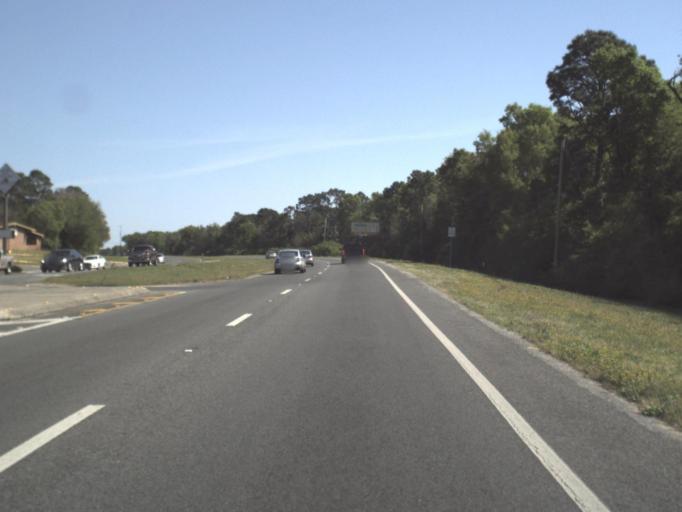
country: US
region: Florida
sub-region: Escambia County
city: Bellview
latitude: 30.4576
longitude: -87.2993
